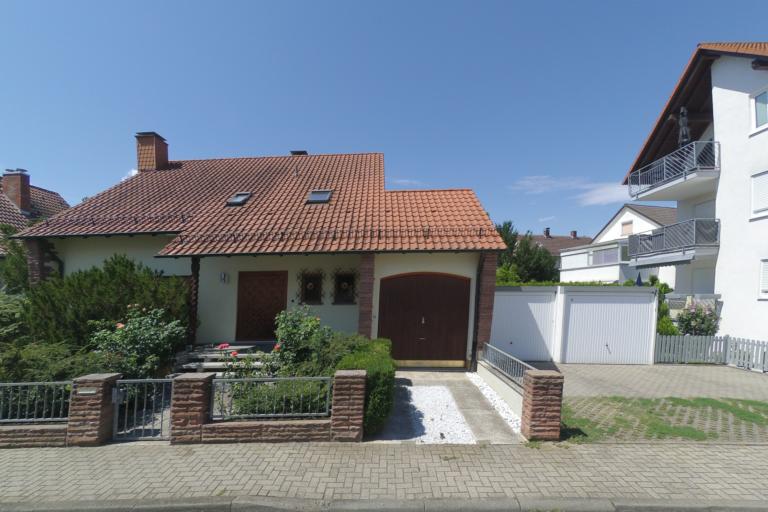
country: DE
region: Rheinland-Pfalz
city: Altrip
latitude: 49.4350
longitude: 8.4999
